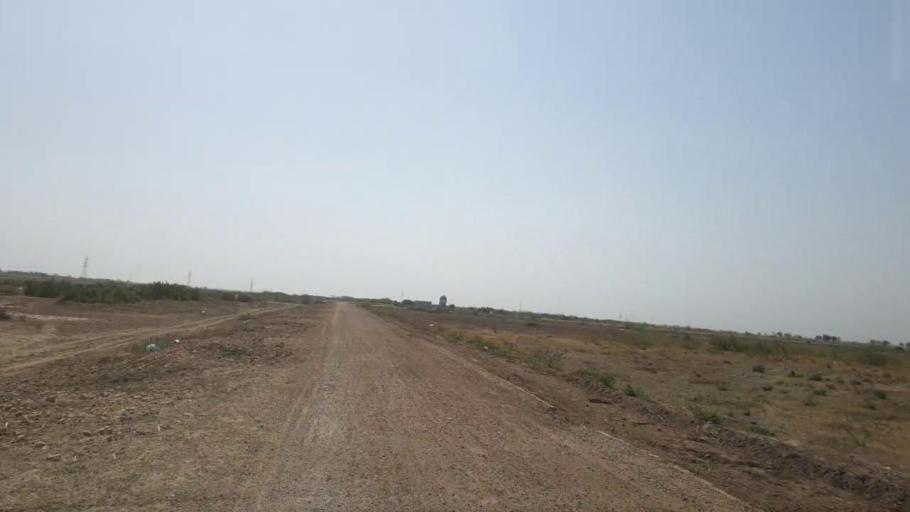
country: PK
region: Sindh
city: Naukot
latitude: 24.9741
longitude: 69.4692
